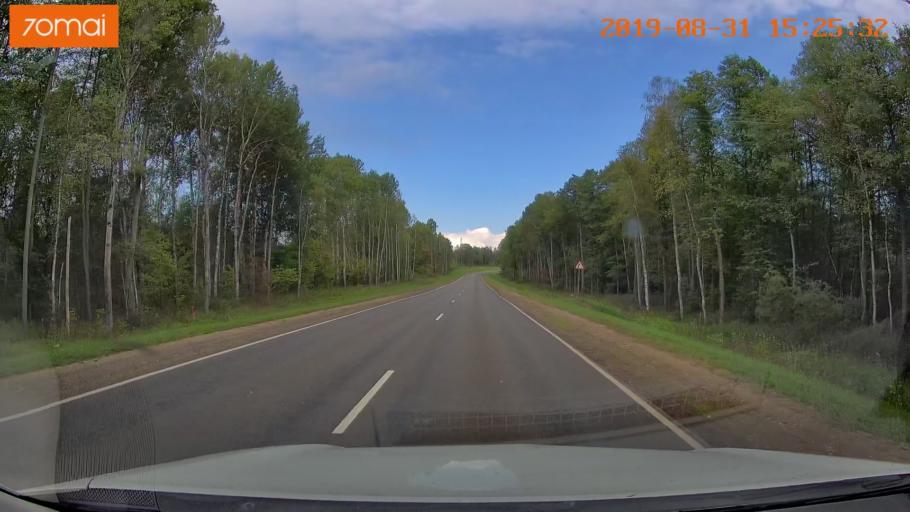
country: RU
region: Kaluga
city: Baryatino
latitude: 54.5426
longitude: 34.5210
